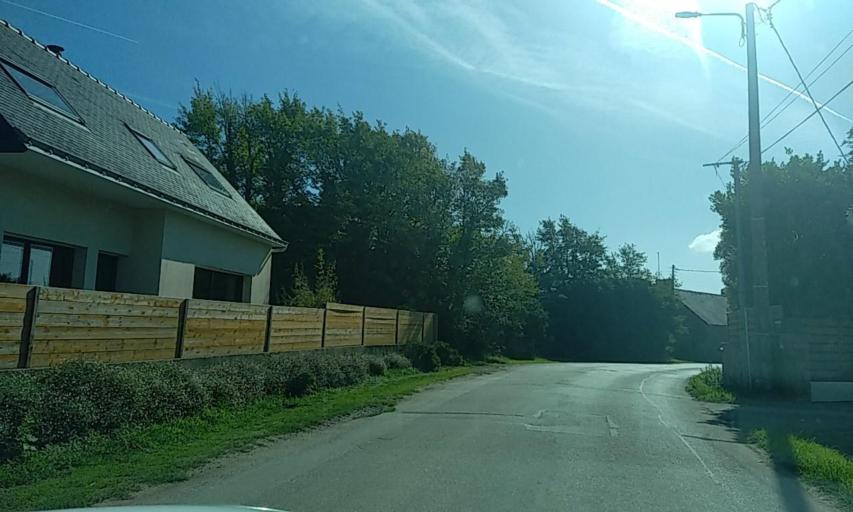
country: FR
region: Brittany
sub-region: Departement du Morbihan
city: Ploemeur
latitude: 47.7163
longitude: -3.4542
